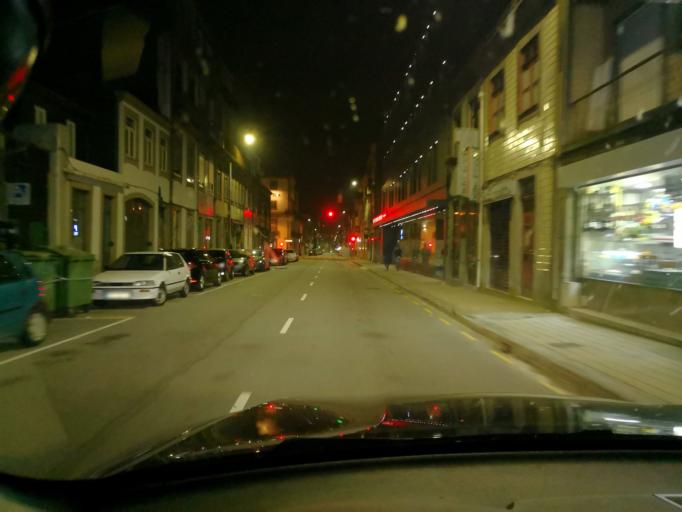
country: PT
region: Porto
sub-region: Porto
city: Porto
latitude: 41.1462
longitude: -8.5940
